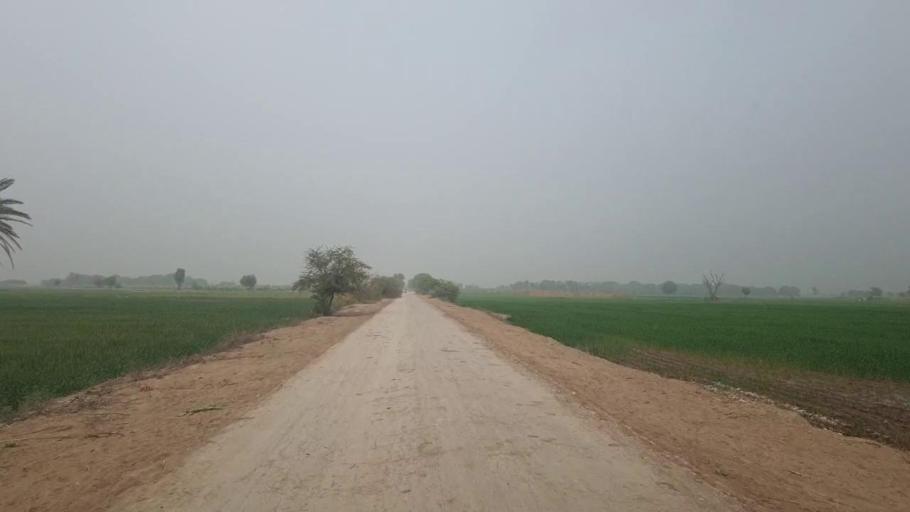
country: PK
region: Sindh
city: Tando Adam
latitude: 25.7594
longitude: 68.7026
